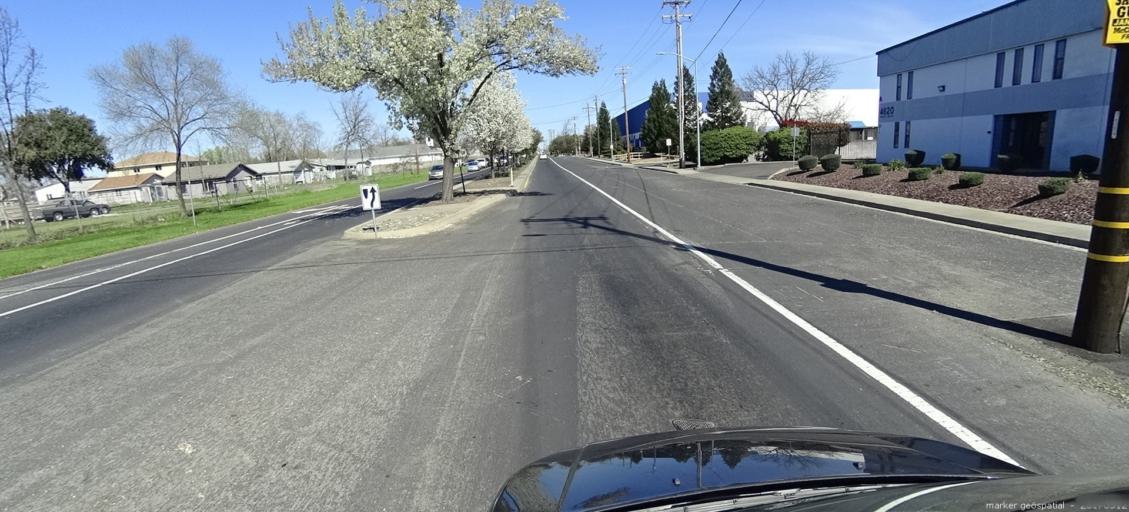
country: US
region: California
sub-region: Sacramento County
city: Rio Linda
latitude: 38.6509
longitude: -121.4291
